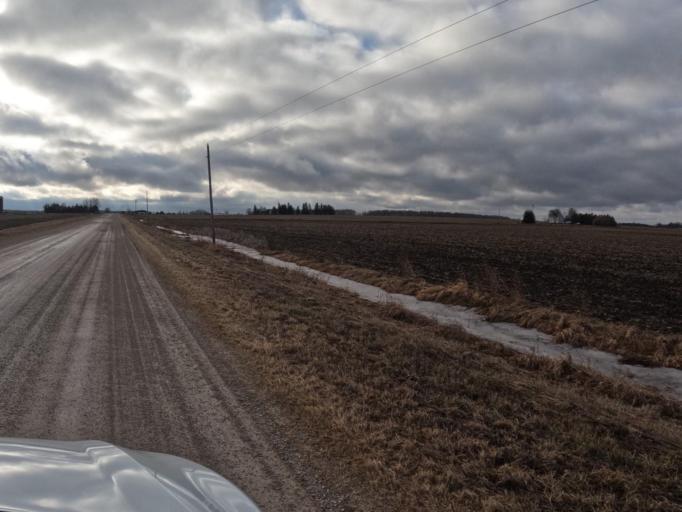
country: CA
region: Ontario
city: Shelburne
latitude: 43.8873
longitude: -80.3594
